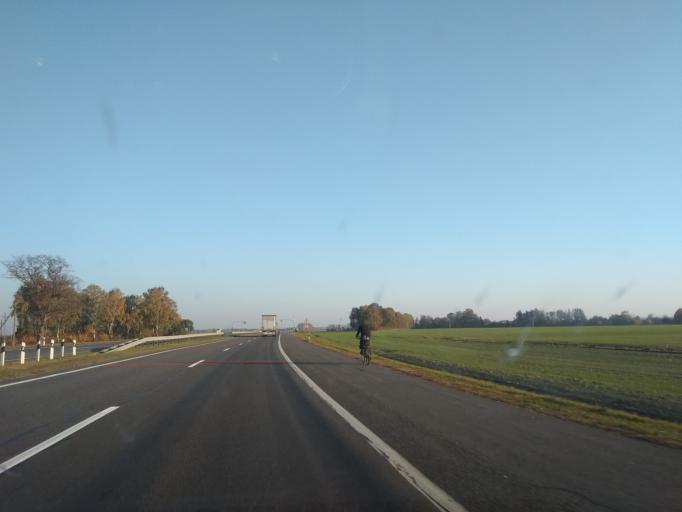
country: BY
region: Brest
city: Kobryn
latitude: 52.1965
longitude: 24.3007
